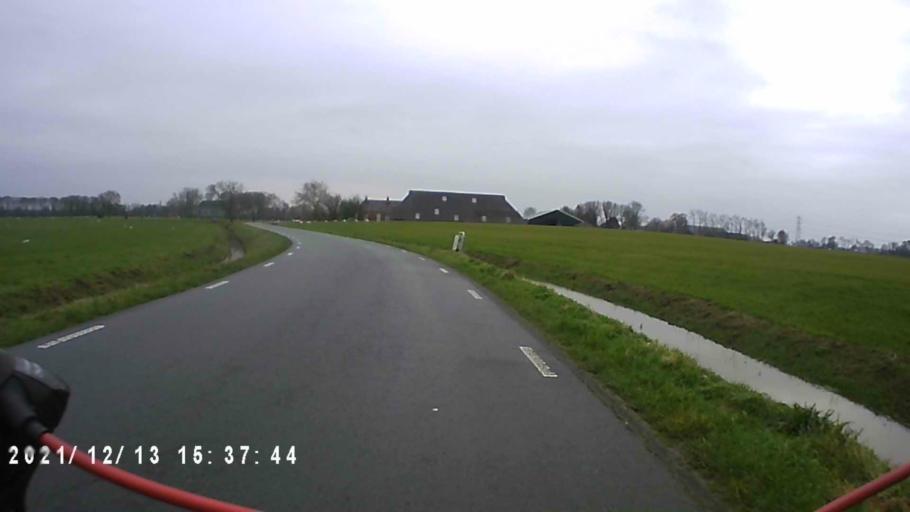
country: NL
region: Groningen
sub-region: Gemeente Appingedam
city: Appingedam
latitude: 53.3272
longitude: 6.8320
